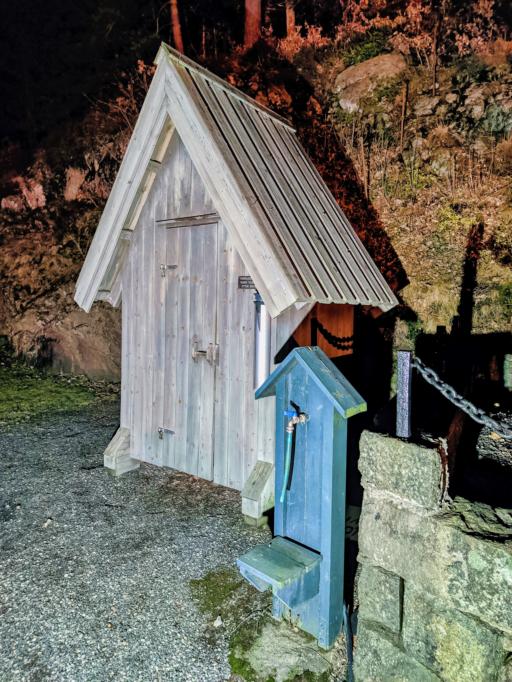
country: NO
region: Aust-Agder
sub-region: Arendal
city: Arendal
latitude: 58.4336
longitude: 8.7484
